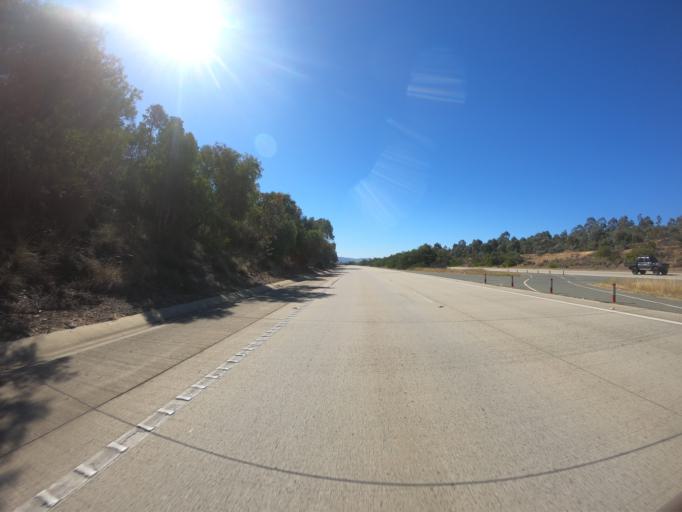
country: AU
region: New South Wales
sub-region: Yass Valley
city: Gundaroo
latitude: -35.1081
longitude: 149.3700
